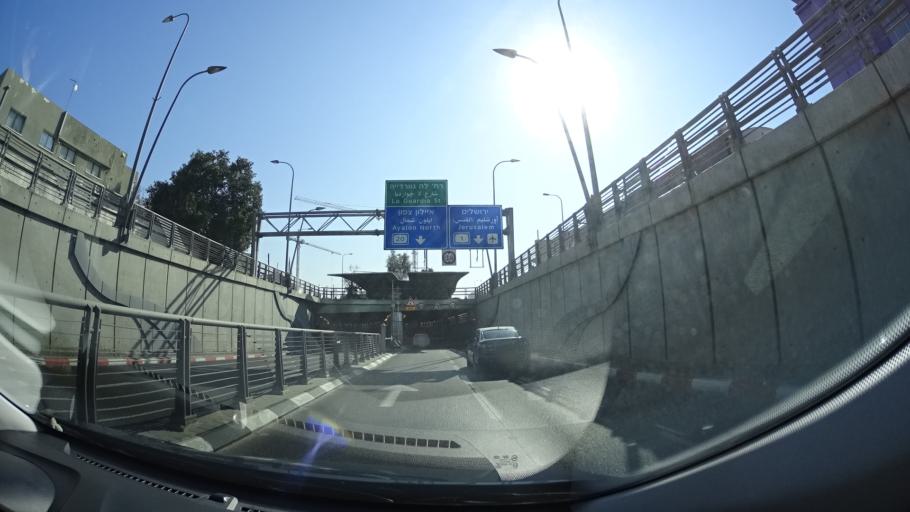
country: IL
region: Tel Aviv
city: Tel Aviv
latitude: 32.0611
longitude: 34.7816
